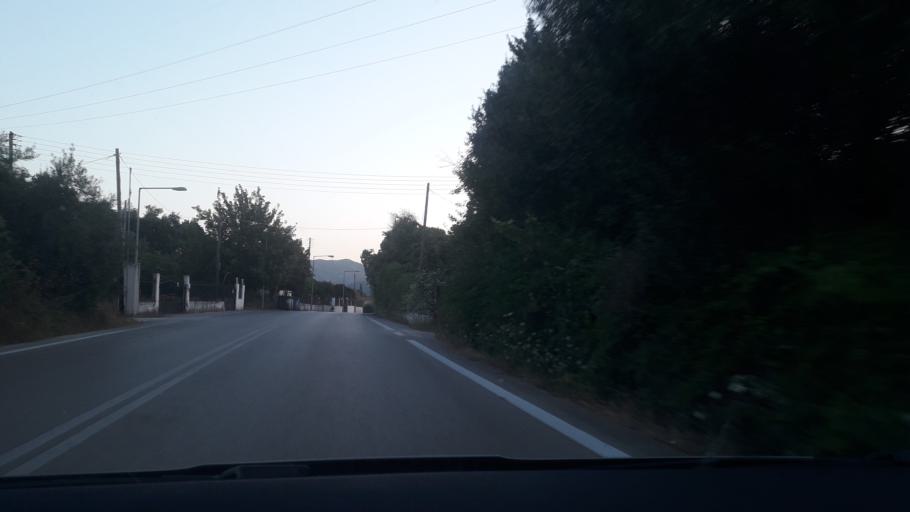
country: GR
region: Ionian Islands
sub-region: Nomos Kerkyras
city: Agios Matthaios
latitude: 39.4635
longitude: 19.9127
